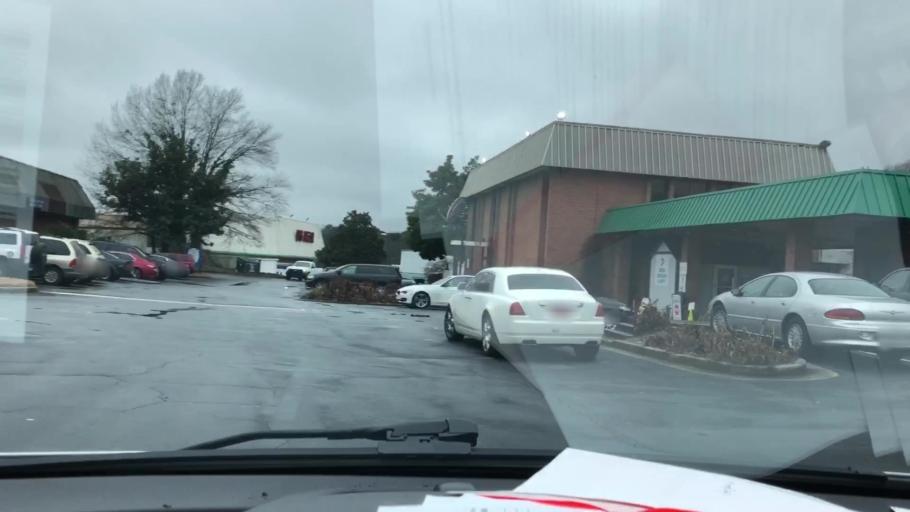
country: US
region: Georgia
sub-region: DeKalb County
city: Panthersville
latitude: 33.7066
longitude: -84.2722
